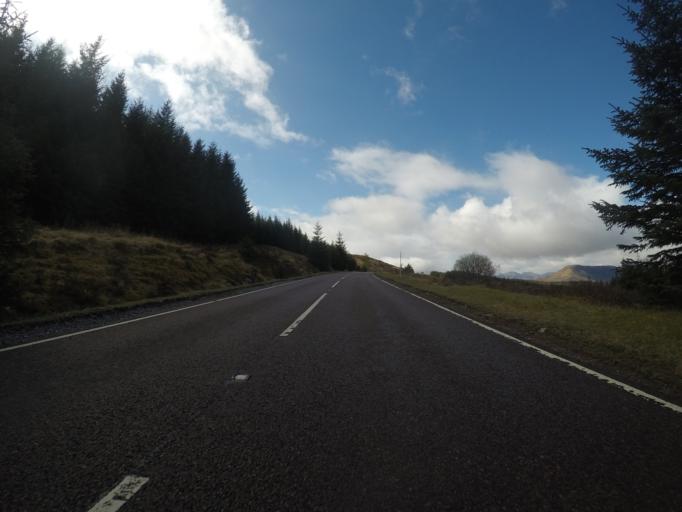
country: GB
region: Scotland
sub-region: Highland
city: Spean Bridge
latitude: 57.1048
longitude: -4.9867
